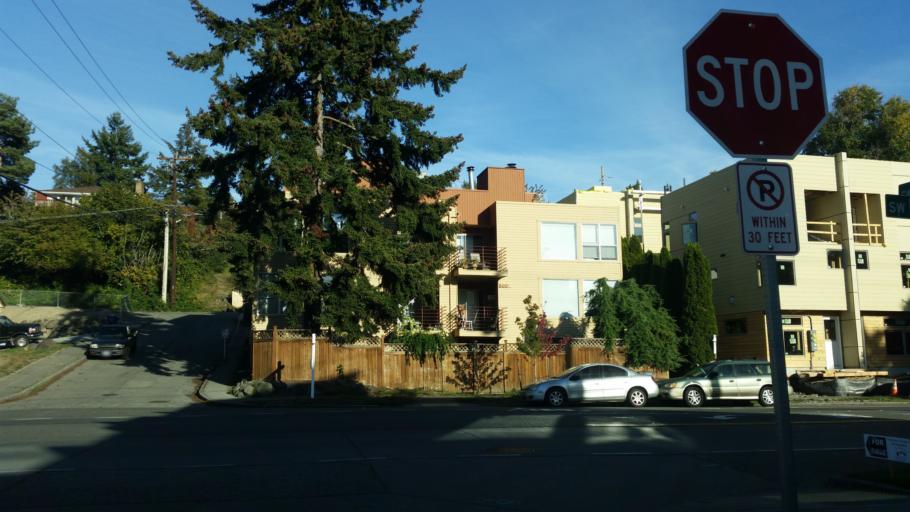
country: US
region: Washington
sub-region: King County
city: White Center
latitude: 47.5574
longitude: -122.3817
